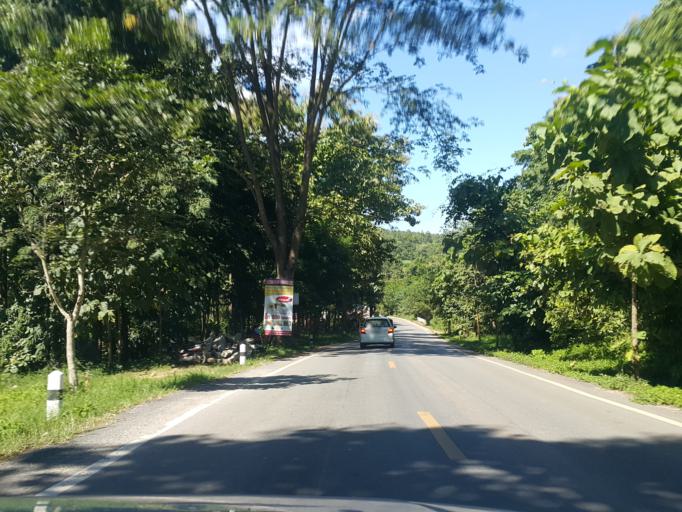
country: TH
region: Chiang Mai
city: Mae Taeng
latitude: 19.1765
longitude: 98.9159
